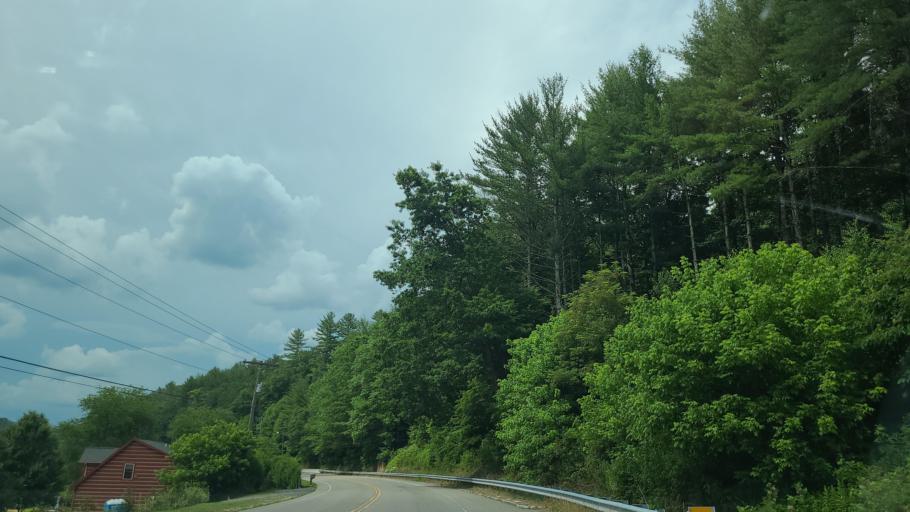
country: US
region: North Carolina
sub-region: Ashe County
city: Jefferson
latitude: 36.3829
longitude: -81.4003
